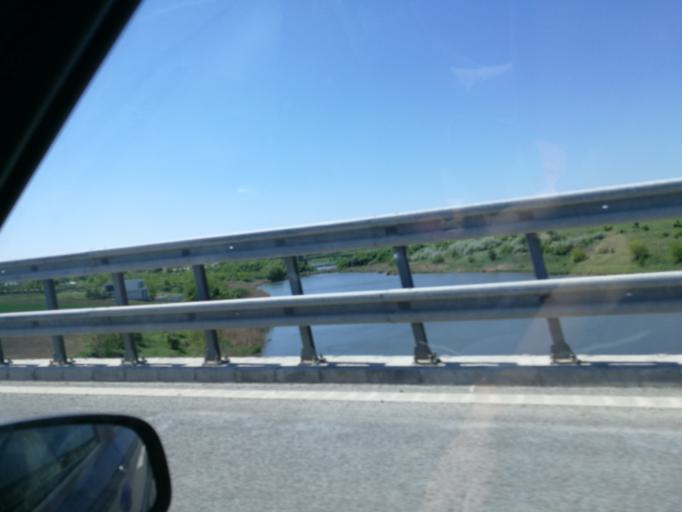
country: RO
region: Ilfov
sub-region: Comuna Moara Vlasiei
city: Caciulati
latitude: 44.6372
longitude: 26.1861
